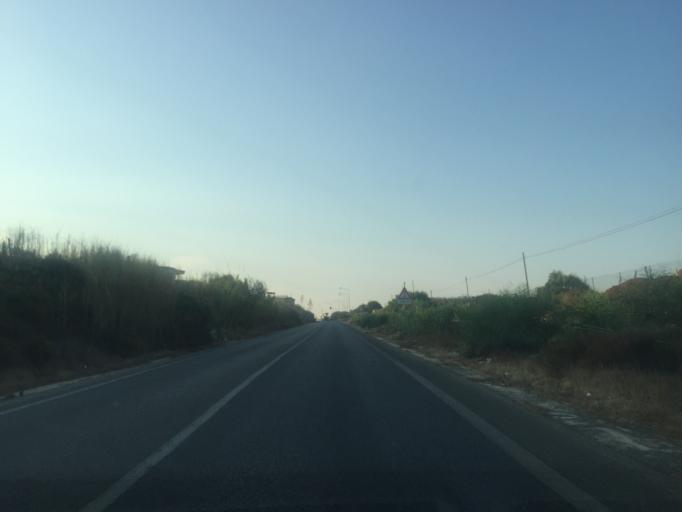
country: IT
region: Sicily
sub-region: Ragusa
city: Cava d'Aliga
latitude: 36.7173
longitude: 14.7569
